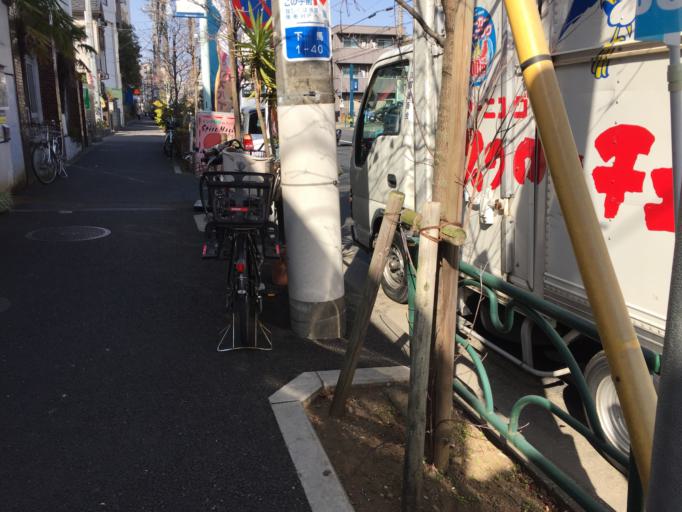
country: JP
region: Tokyo
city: Tokyo
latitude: 35.6410
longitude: 139.6816
